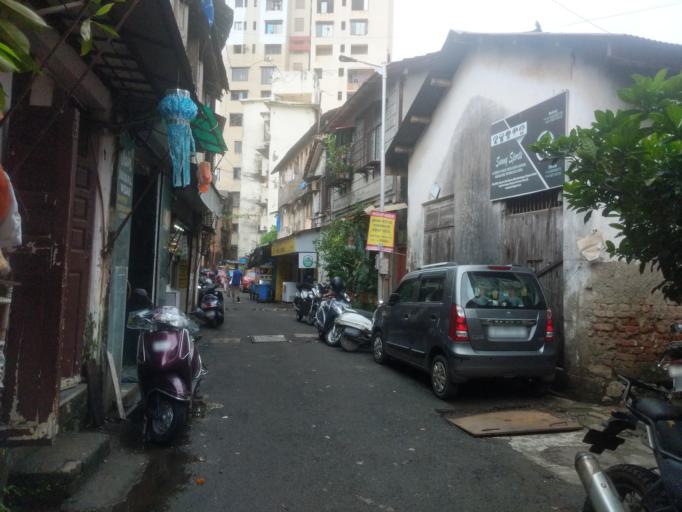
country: IN
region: Maharashtra
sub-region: Mumbai Suburban
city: Mumbai
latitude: 18.9510
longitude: 72.8248
